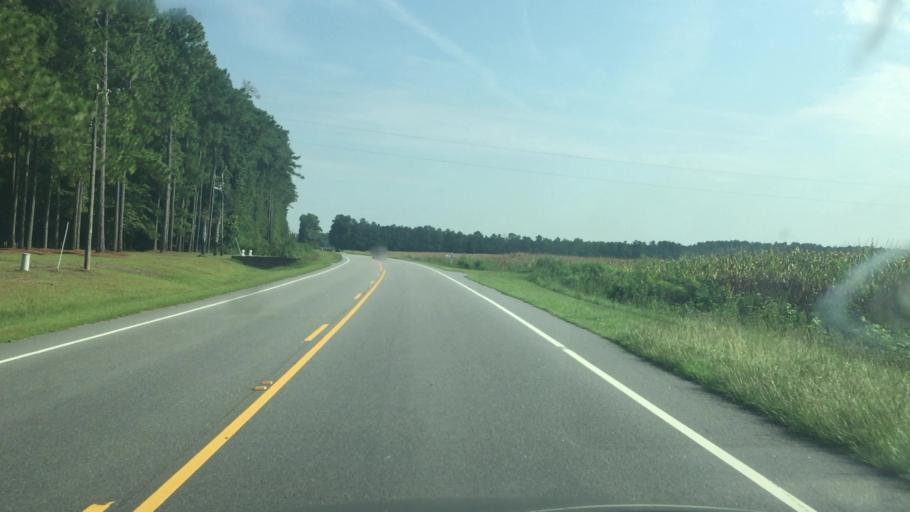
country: US
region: North Carolina
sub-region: Columbus County
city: Tabor City
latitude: 34.1759
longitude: -78.8404
